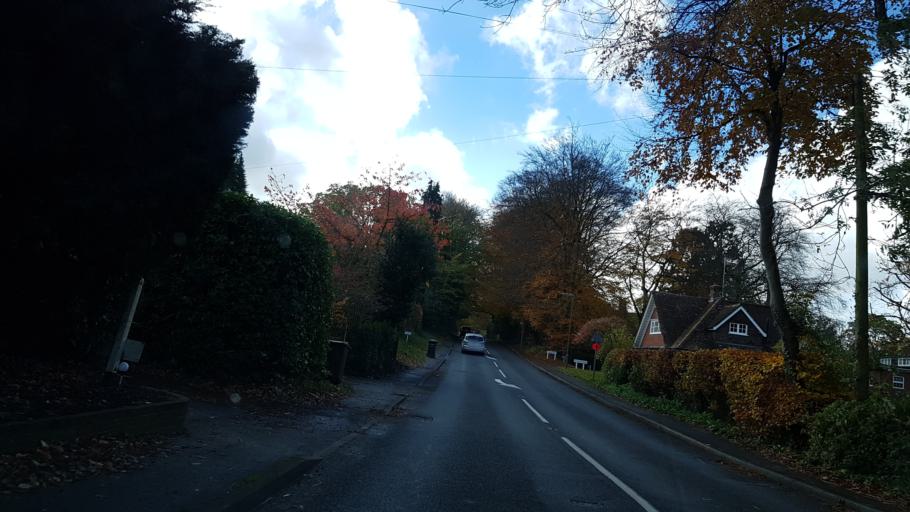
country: GB
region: England
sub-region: Surrey
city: Haslemere
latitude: 51.0964
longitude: -0.7023
